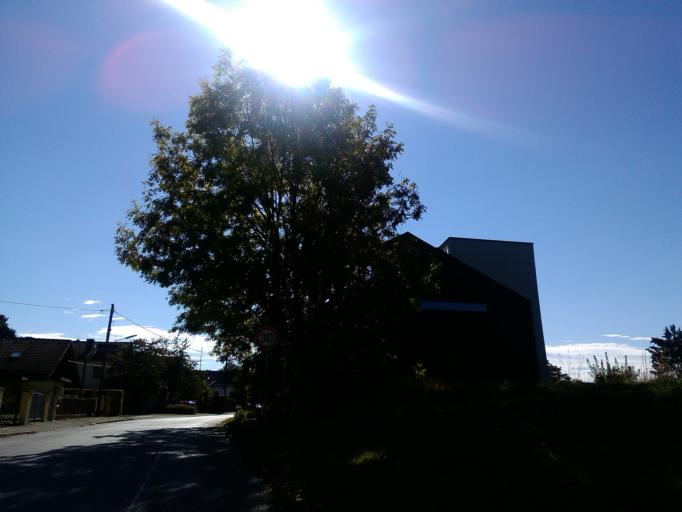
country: DE
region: Bavaria
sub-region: Upper Bavaria
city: Gauting
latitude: 48.0604
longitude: 11.4040
